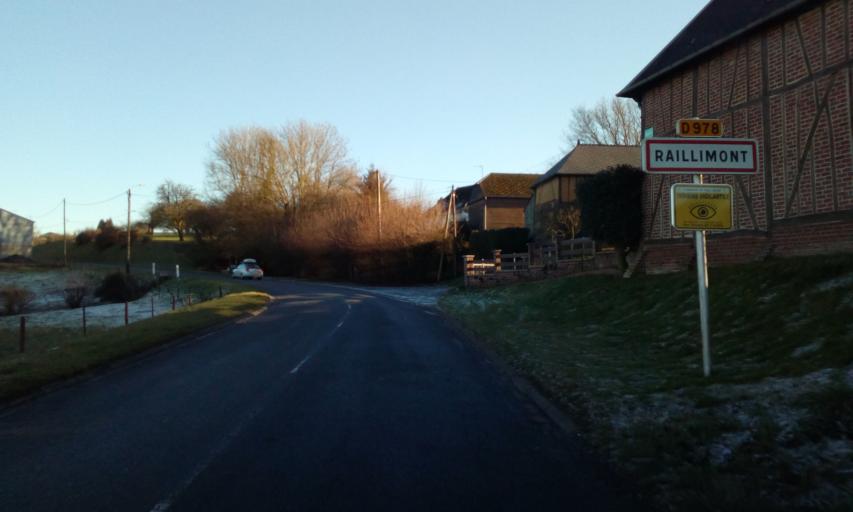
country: FR
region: Picardie
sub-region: Departement de l'Aisne
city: Rozoy-sur-Serre
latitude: 49.7074
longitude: 4.1454
